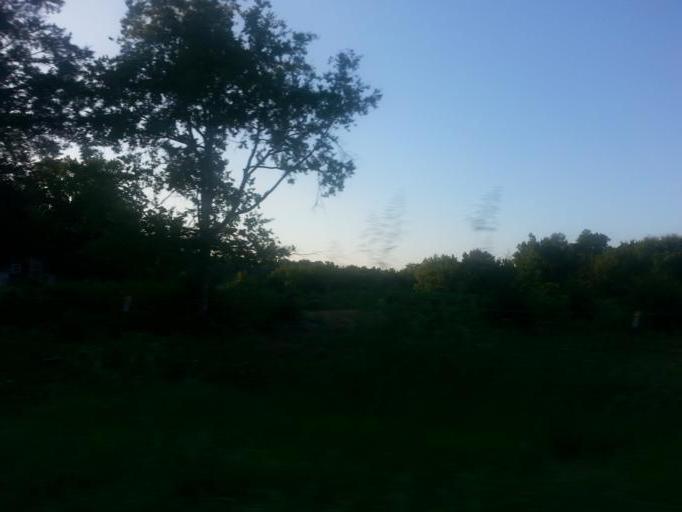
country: US
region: Tennessee
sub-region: Jefferson County
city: New Market
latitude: 36.0216
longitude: -83.5424
